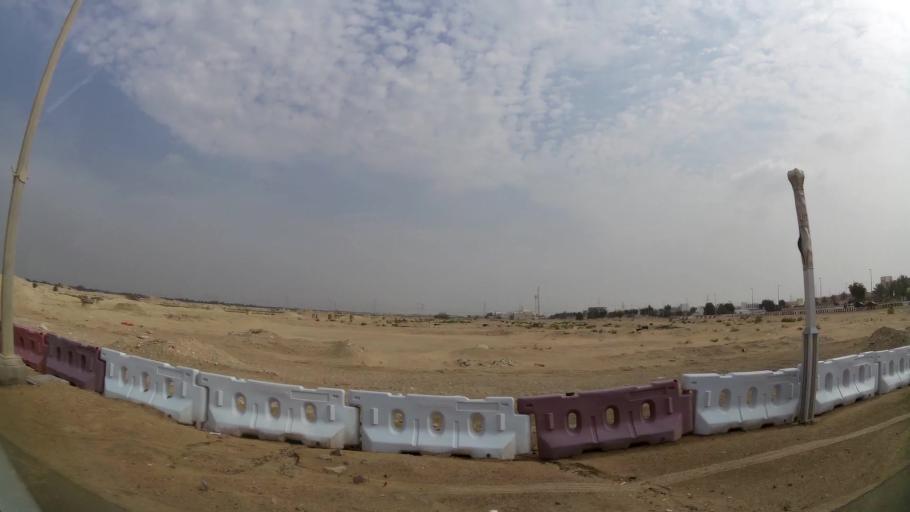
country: AE
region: Abu Dhabi
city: Abu Dhabi
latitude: 24.6501
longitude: 54.7349
